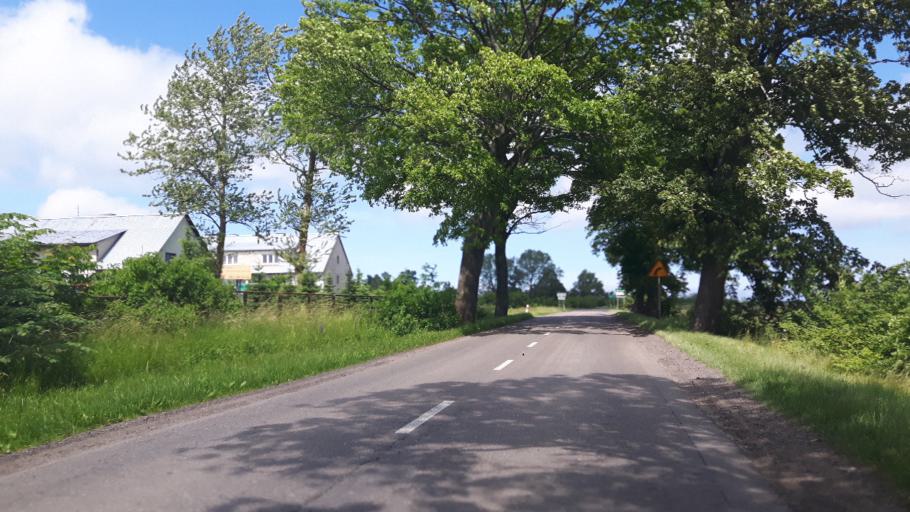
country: PL
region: Pomeranian Voivodeship
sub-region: Powiat slupski
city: Ustka
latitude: 54.5432
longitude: 16.8239
